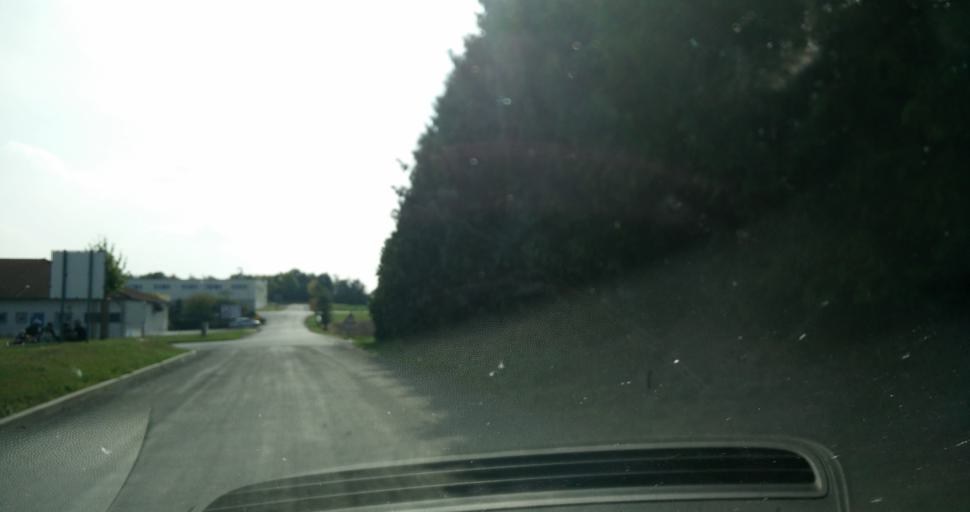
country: DE
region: Saxony
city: Colditz
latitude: 51.1390
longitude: 12.7915
